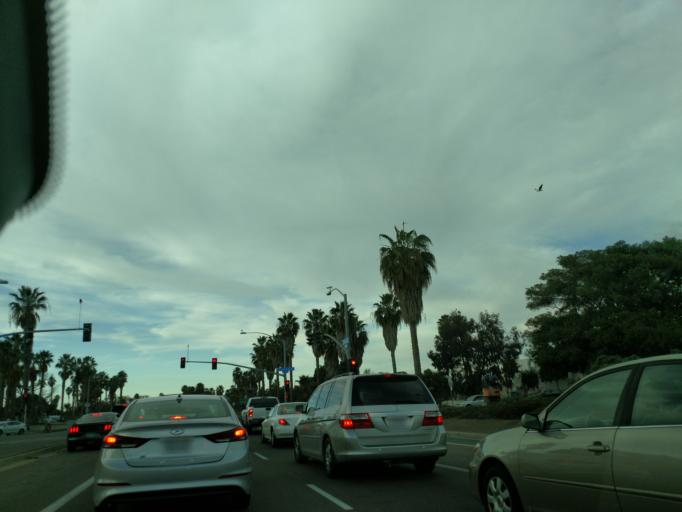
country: US
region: California
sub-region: San Diego County
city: Coronado
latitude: 32.7508
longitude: -117.2358
